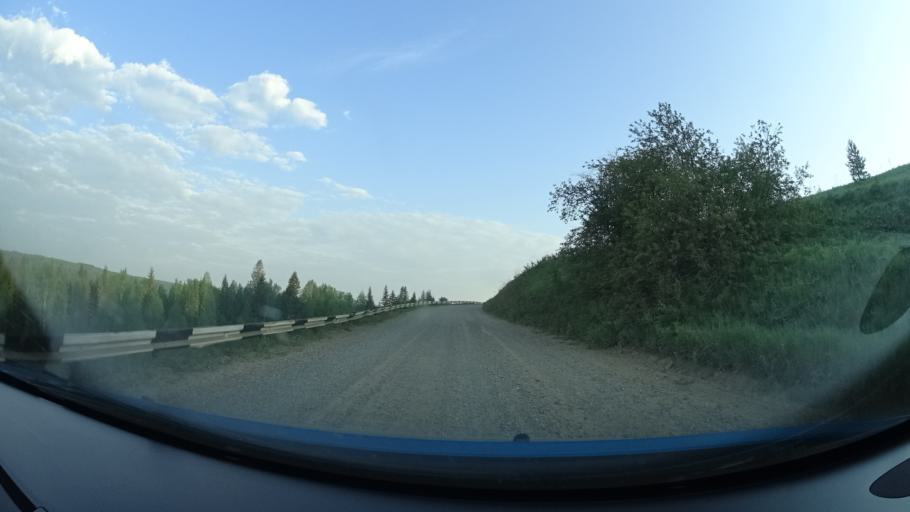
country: RU
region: Perm
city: Kuyeda
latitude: 56.6471
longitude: 55.7014
